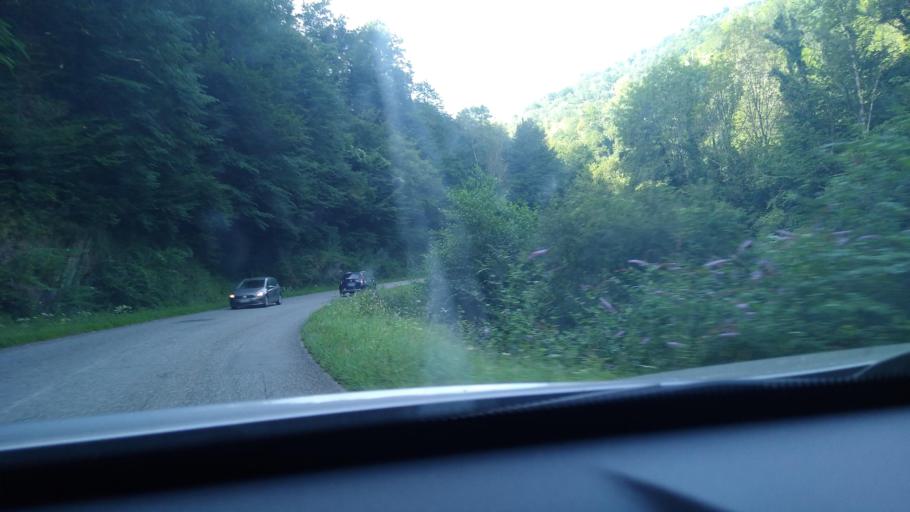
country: FR
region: Midi-Pyrenees
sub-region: Departement de l'Ariege
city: Saint-Girons
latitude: 42.8501
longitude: 1.1927
